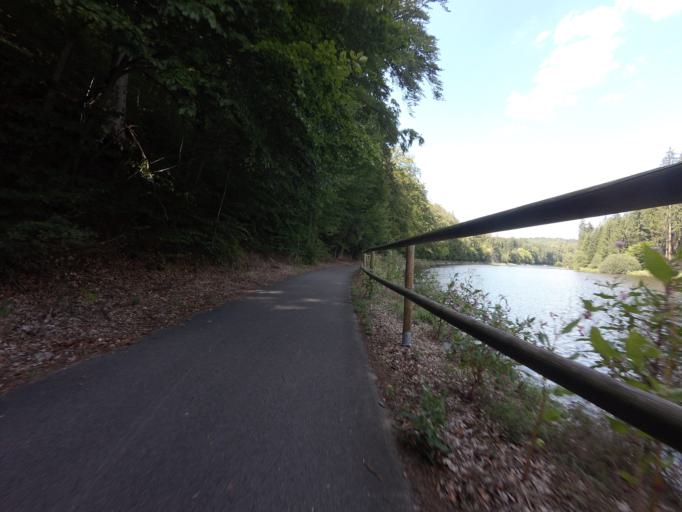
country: CZ
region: Jihocesky
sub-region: Okres Ceske Budejovice
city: Hluboka nad Vltavou
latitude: 49.0735
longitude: 14.4534
